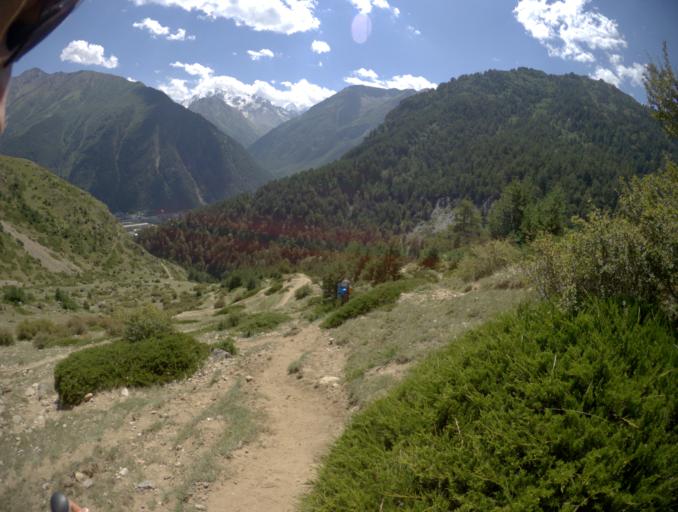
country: RU
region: Kabardino-Balkariya
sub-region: El'brusskiy Rayon
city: El'brus
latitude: 43.2659
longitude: 42.6348
